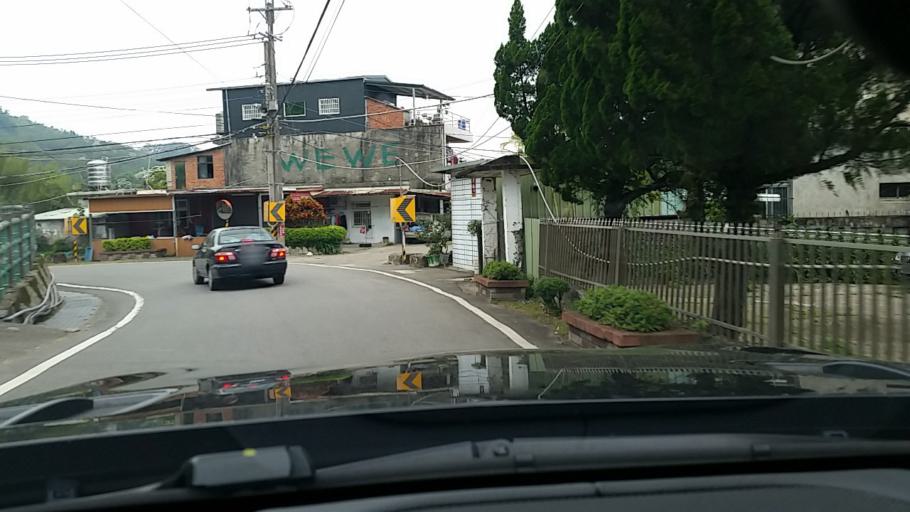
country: TW
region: Taiwan
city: Daxi
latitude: 24.8006
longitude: 121.3056
